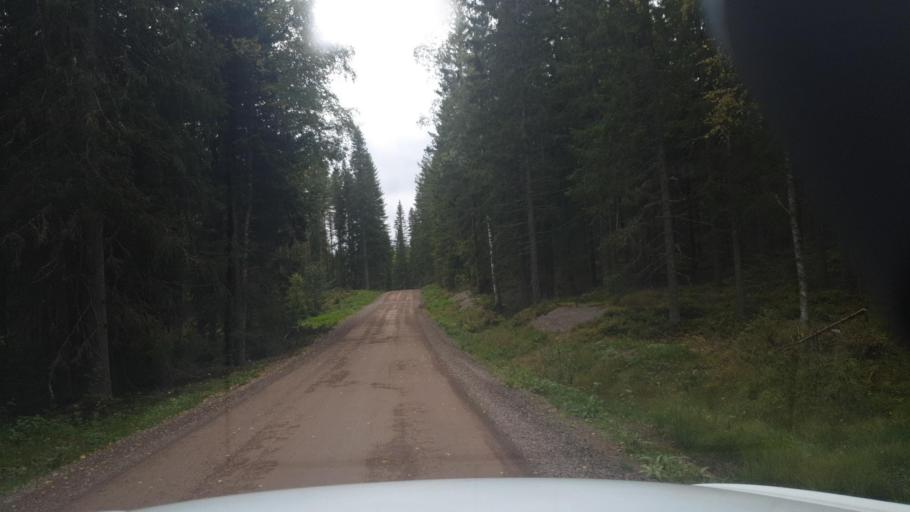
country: SE
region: Vaermland
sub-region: Arvika Kommun
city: Arvika
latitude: 59.9655
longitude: 12.6595
